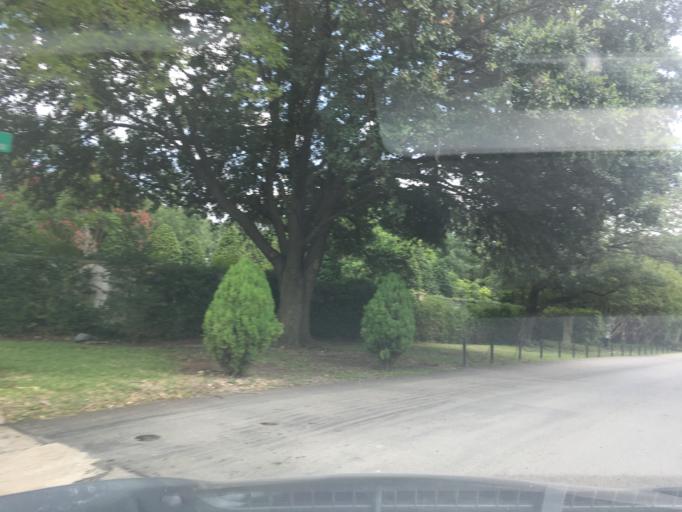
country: US
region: Texas
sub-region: Dallas County
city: University Park
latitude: 32.8948
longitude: -96.8248
